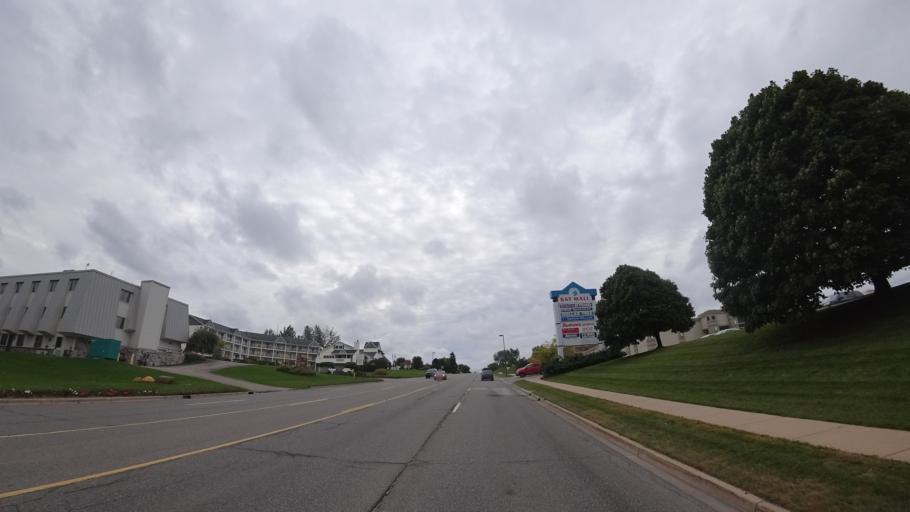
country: US
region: Michigan
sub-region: Emmet County
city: Petoskey
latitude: 45.3673
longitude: -84.9710
